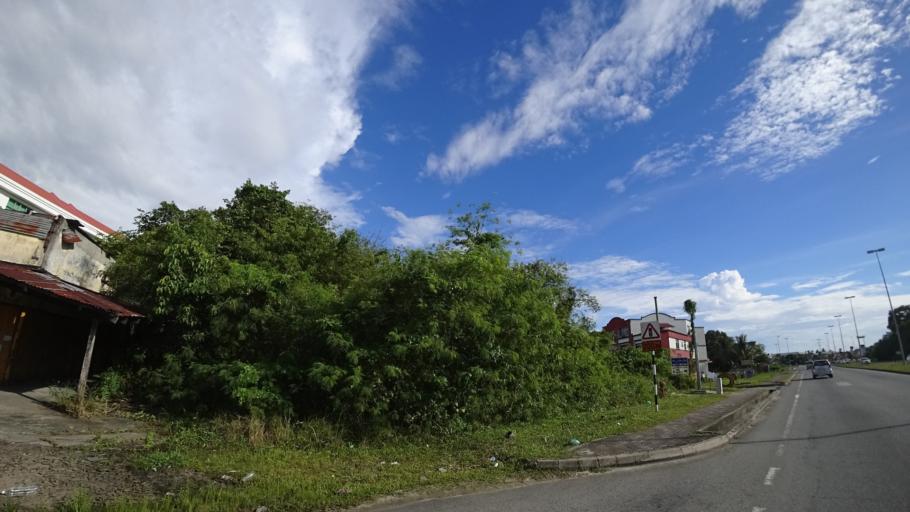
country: BN
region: Brunei and Muara
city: Bandar Seri Begawan
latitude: 4.8913
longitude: 114.8461
